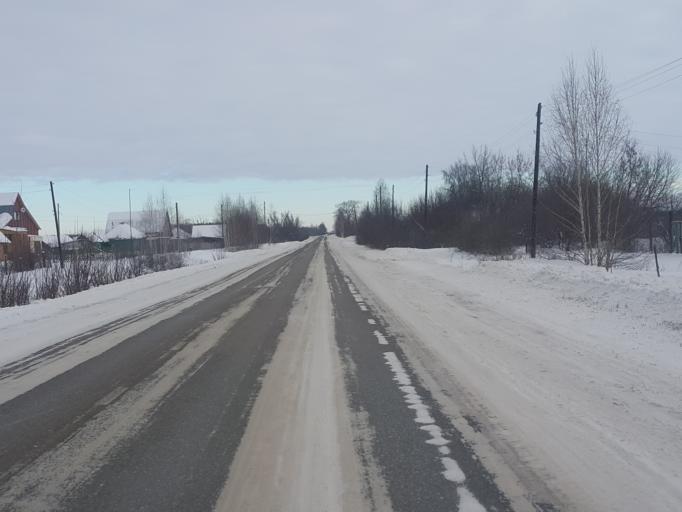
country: RU
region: Tambov
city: Platonovka
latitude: 52.8632
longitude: 41.8468
